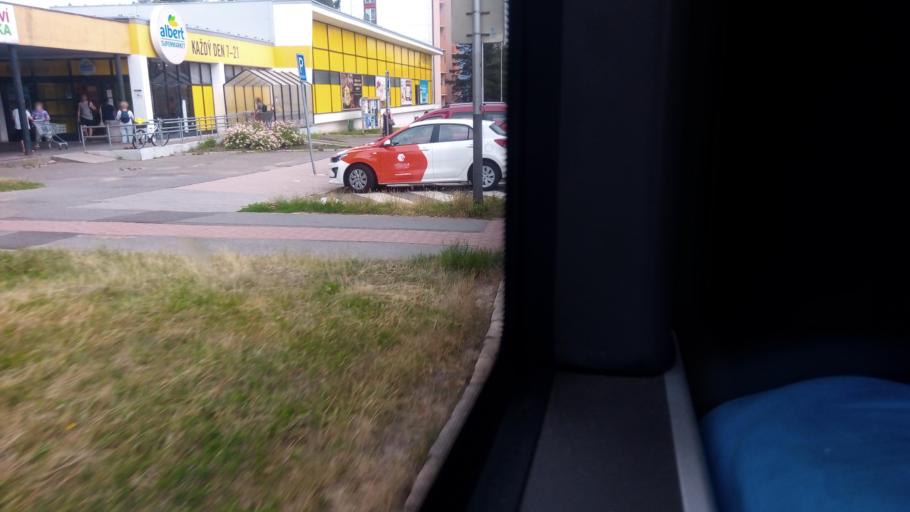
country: CZ
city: Vresina
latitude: 49.8363
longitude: 18.1830
